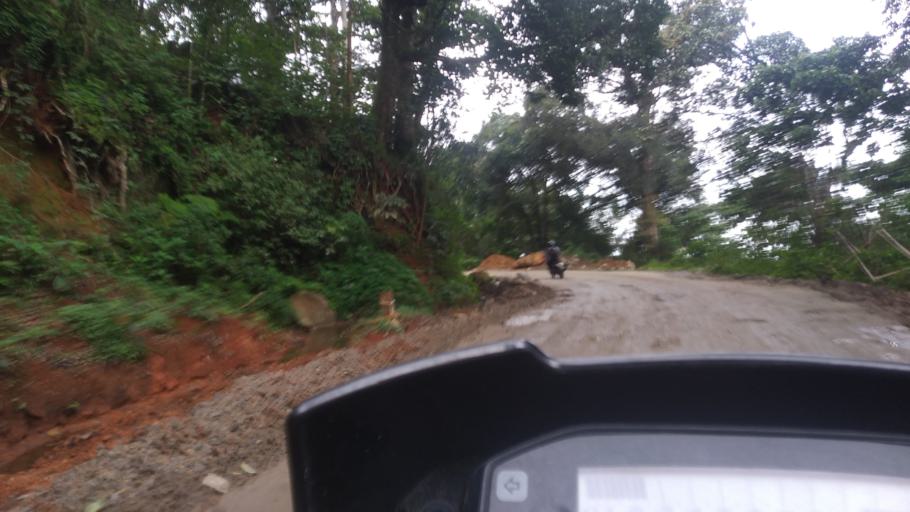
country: IN
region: Kerala
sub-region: Idukki
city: Munnar
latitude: 10.0358
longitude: 77.1407
